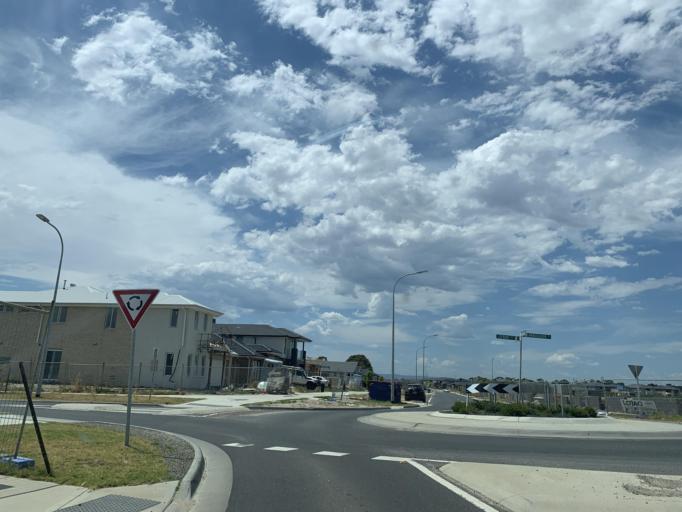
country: AU
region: Victoria
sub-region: Casey
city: Cranbourne South
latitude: -38.1283
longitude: 145.2346
